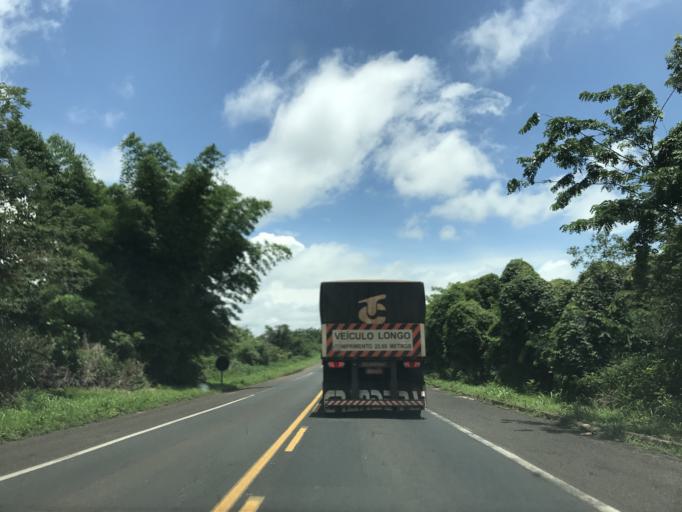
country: BR
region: Minas Gerais
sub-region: Prata
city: Prata
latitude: -19.6411
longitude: -48.9678
